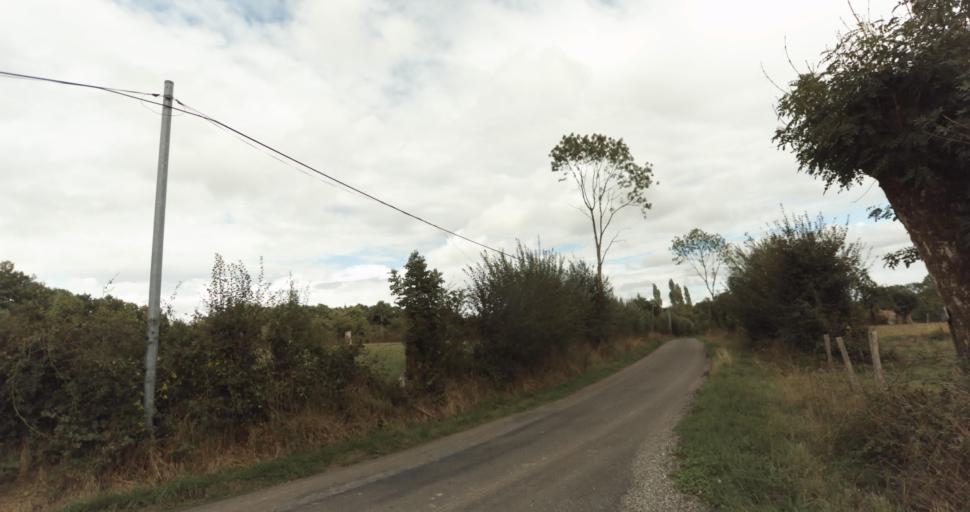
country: FR
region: Lower Normandy
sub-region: Departement de l'Orne
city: Sainte-Gauburge-Sainte-Colombe
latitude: 48.7754
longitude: 0.3776
